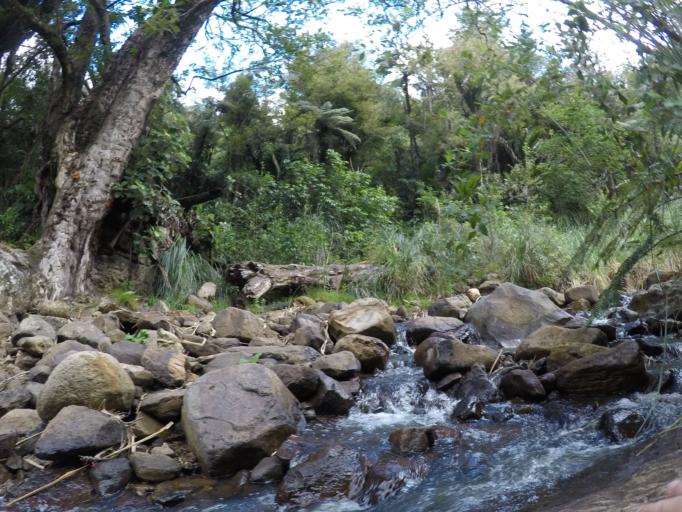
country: NZ
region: Bay of Plenty
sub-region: Western Bay of Plenty District
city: Waihi Beach
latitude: -37.3803
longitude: 175.9290
